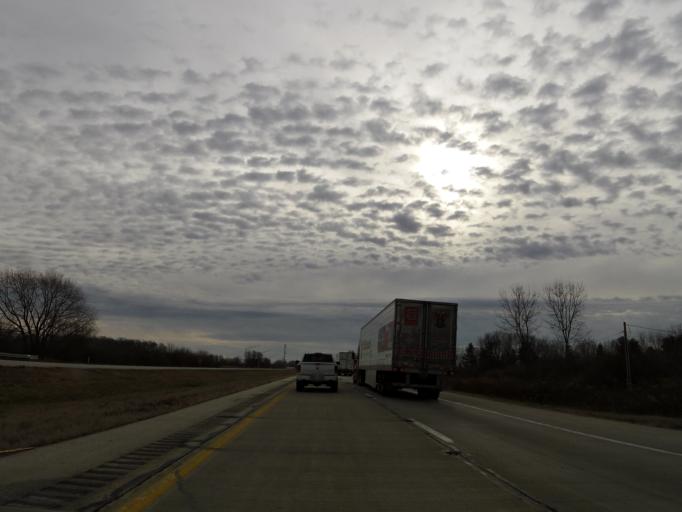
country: US
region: Indiana
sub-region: Hendricks County
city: Pittsboro
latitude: 39.9069
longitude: -86.5622
